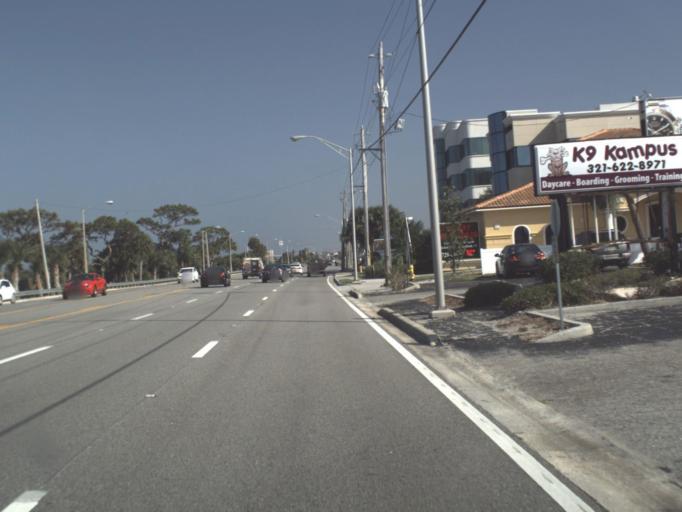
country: US
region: Florida
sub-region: Brevard County
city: Melbourne
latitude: 28.1114
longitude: -80.6188
